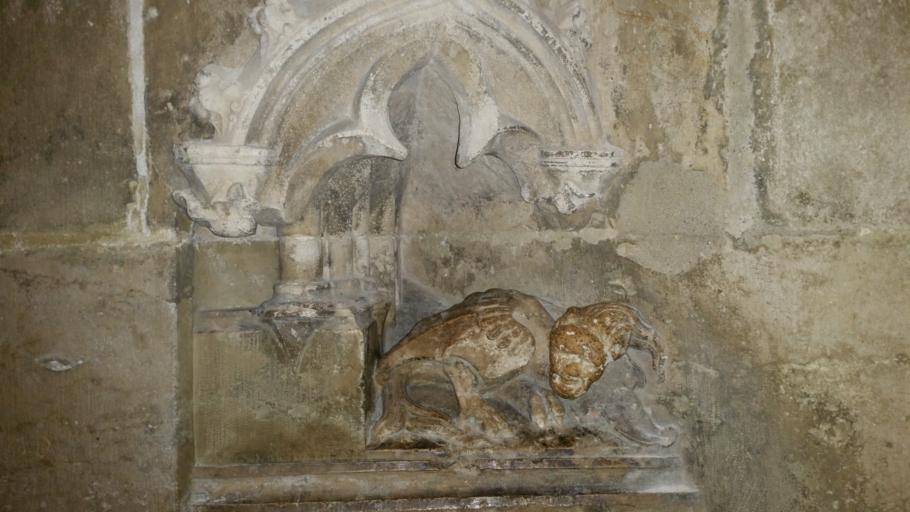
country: DE
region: Bavaria
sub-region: Upper Palatinate
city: Regensburg
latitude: 49.0189
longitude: 12.0986
